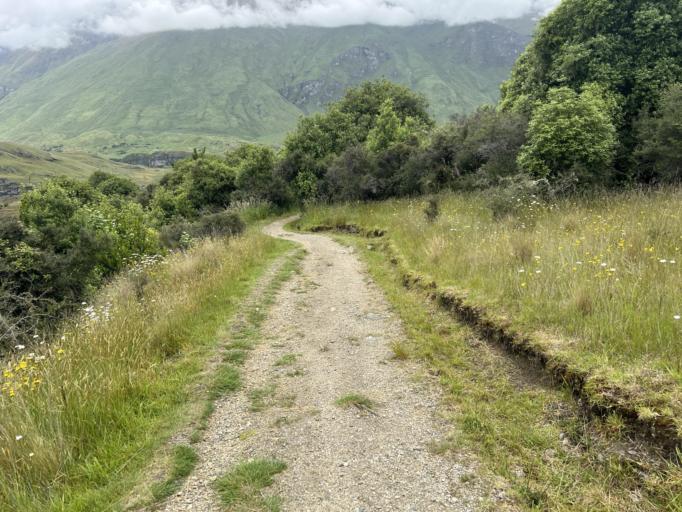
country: NZ
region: Otago
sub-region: Queenstown-Lakes District
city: Wanaka
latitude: -44.6463
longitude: 168.9667
